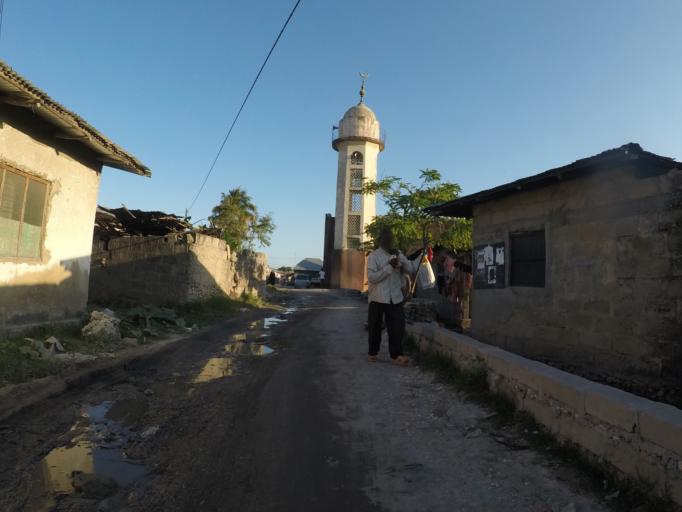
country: TZ
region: Zanzibar Urban/West
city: Zanzibar
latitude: -6.1598
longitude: 39.2178
